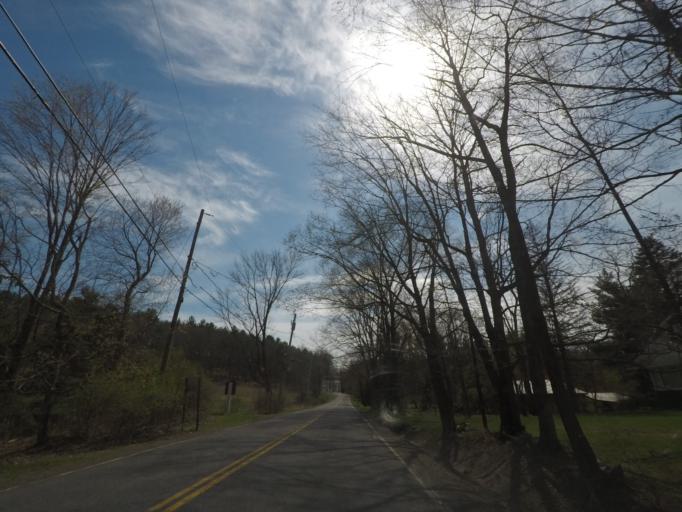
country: US
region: New York
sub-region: Columbia County
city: Chatham
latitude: 42.3640
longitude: -73.5321
